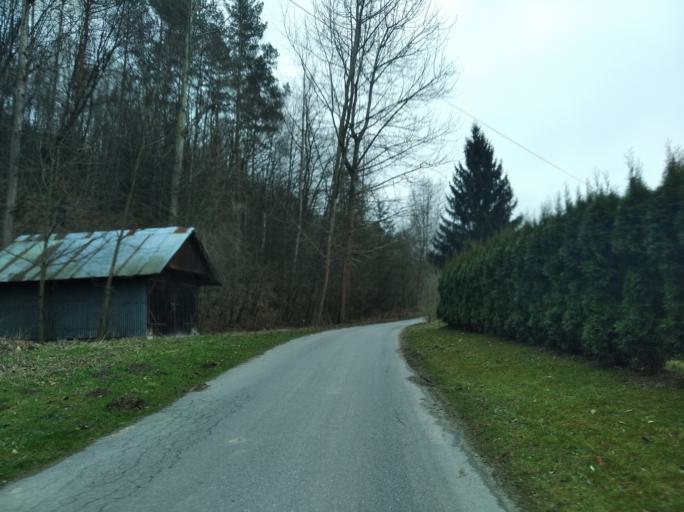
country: PL
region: Subcarpathian Voivodeship
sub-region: Powiat strzyzowski
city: Strzyzow
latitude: 49.8602
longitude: 21.8322
